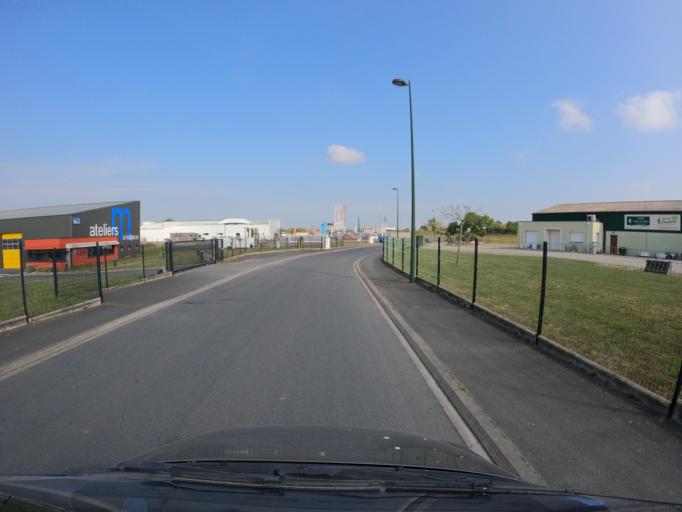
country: FR
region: Pays de la Loire
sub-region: Departement de la Vendee
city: La Bruffiere
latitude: 47.0062
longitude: -1.1901
